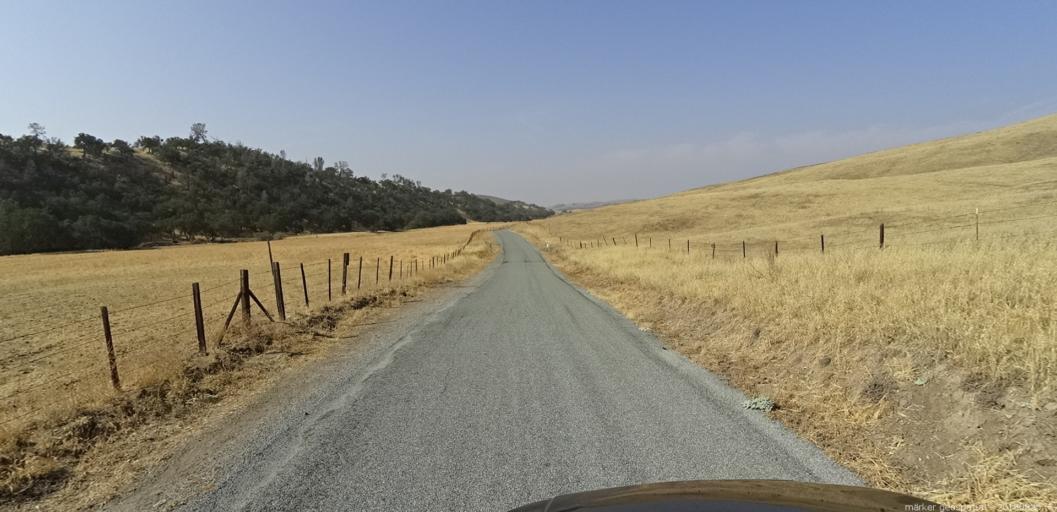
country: US
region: California
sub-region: San Luis Obispo County
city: San Miguel
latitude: 35.8156
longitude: -120.5226
